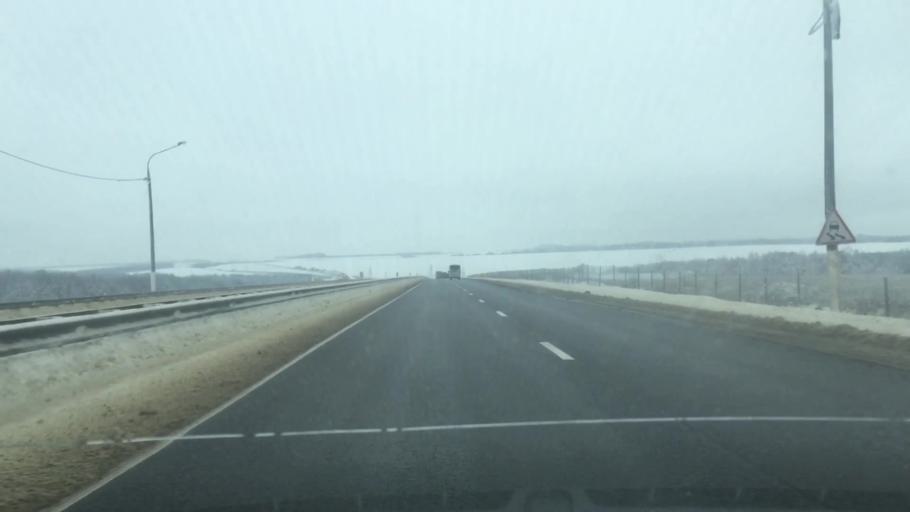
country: RU
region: Tula
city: Kazachka
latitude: 53.2864
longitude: 38.1790
